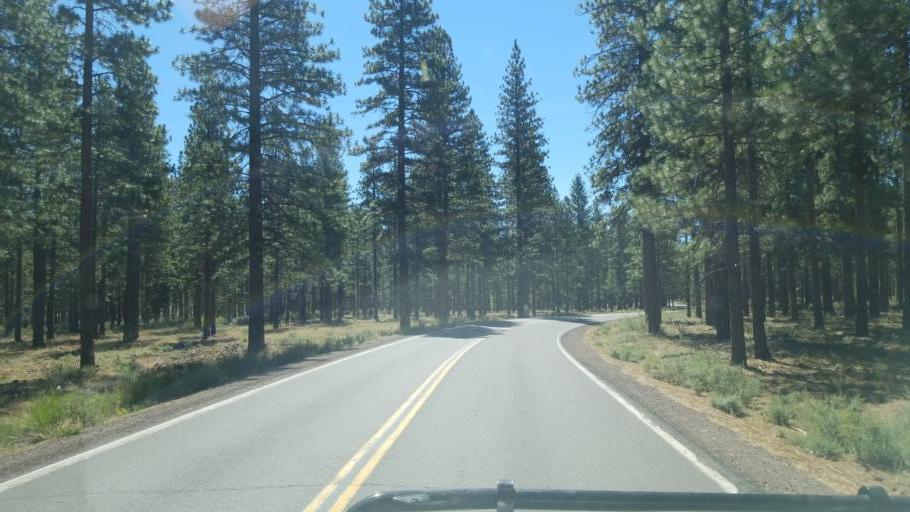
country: US
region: California
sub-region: Lassen County
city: Susanville
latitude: 40.4252
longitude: -120.7238
